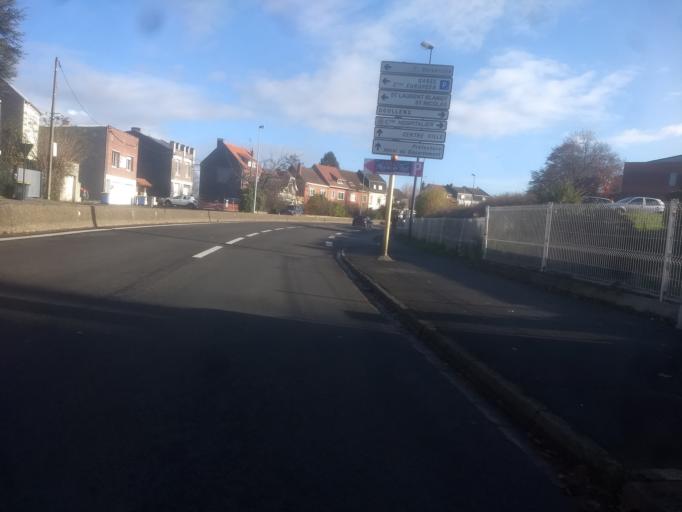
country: FR
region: Nord-Pas-de-Calais
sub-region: Departement du Pas-de-Calais
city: Sainte-Catherine
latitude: 50.2979
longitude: 2.7596
